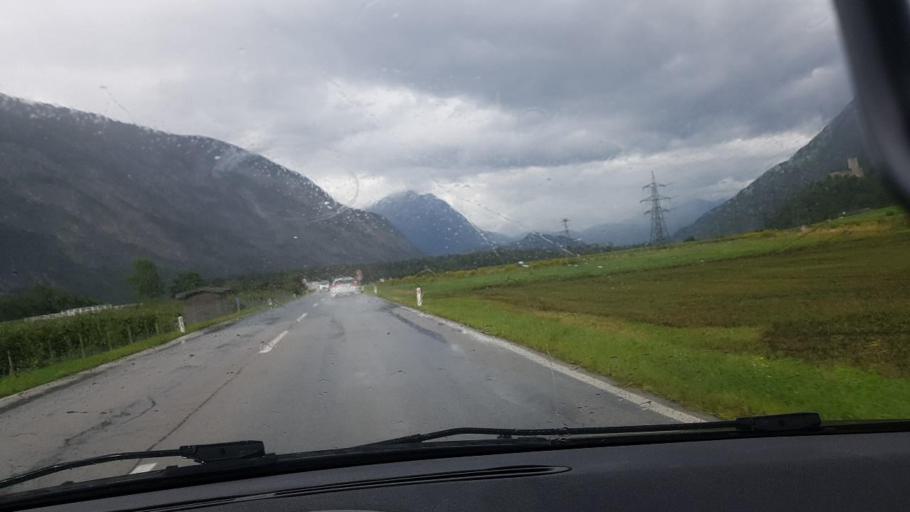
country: AT
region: Tyrol
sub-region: Politischer Bezirk Imst
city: Haiming
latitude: 47.2543
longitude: 10.8935
